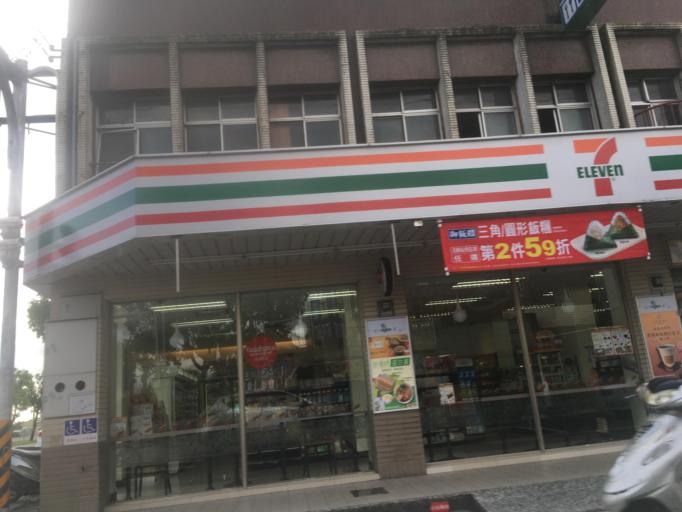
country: TW
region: Taiwan
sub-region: Yilan
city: Yilan
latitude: 24.6940
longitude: 121.7302
